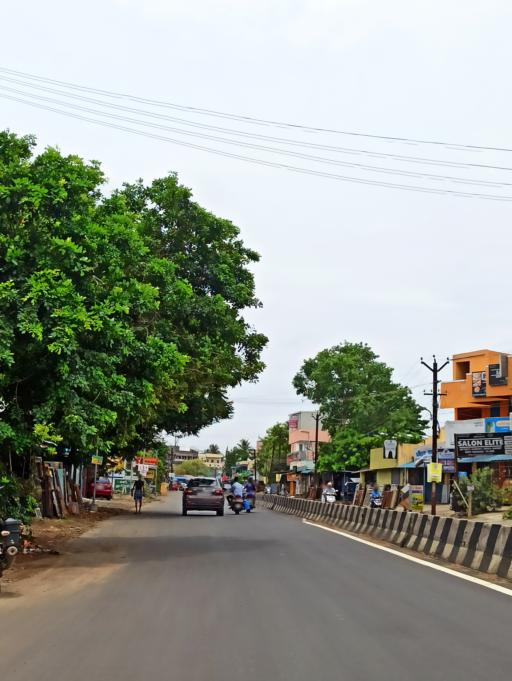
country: IN
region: Tamil Nadu
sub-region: Kancheepuram
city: Vandalur
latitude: 12.9160
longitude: 80.0789
